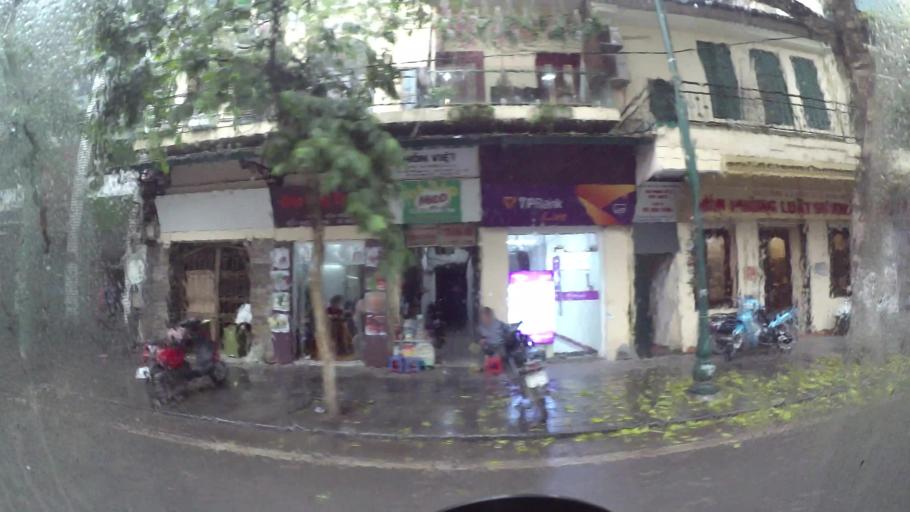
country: VN
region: Ha Noi
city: Hoan Kiem
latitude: 21.0262
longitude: 105.8506
